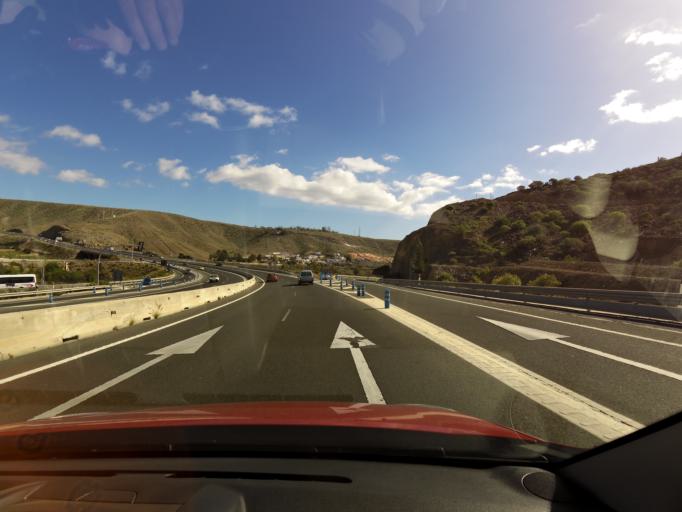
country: ES
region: Canary Islands
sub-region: Provincia de Las Palmas
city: Puerto Rico
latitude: 27.7662
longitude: -15.6738
